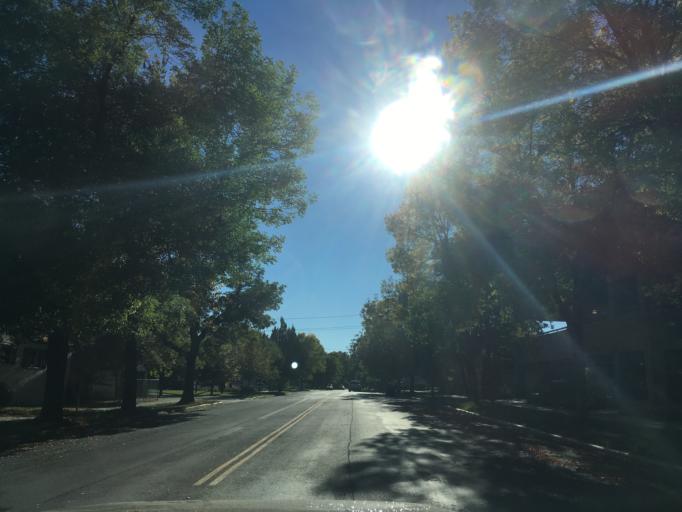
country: US
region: Montana
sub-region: Yellowstone County
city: Billings
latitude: 45.7915
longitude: -108.5168
